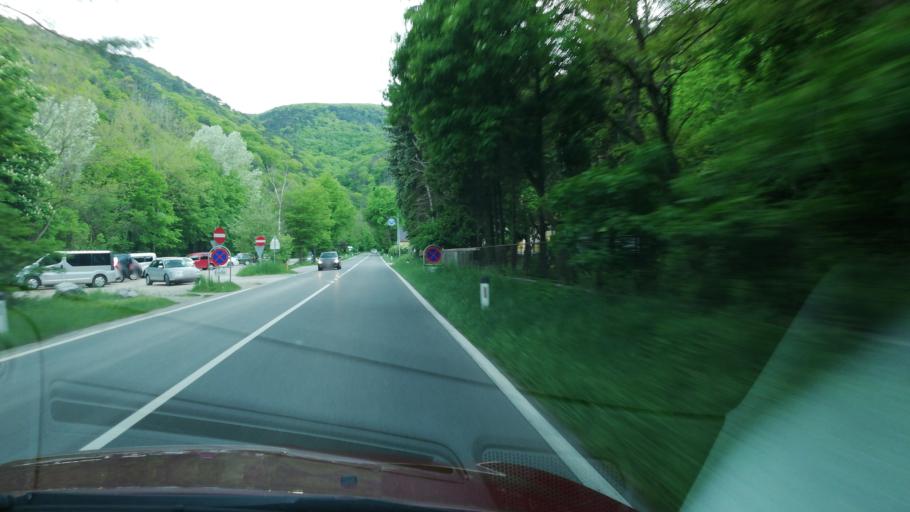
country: AT
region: Lower Austria
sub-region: Politischer Bezirk Modling
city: Gaaden
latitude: 48.0142
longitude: 16.1713
